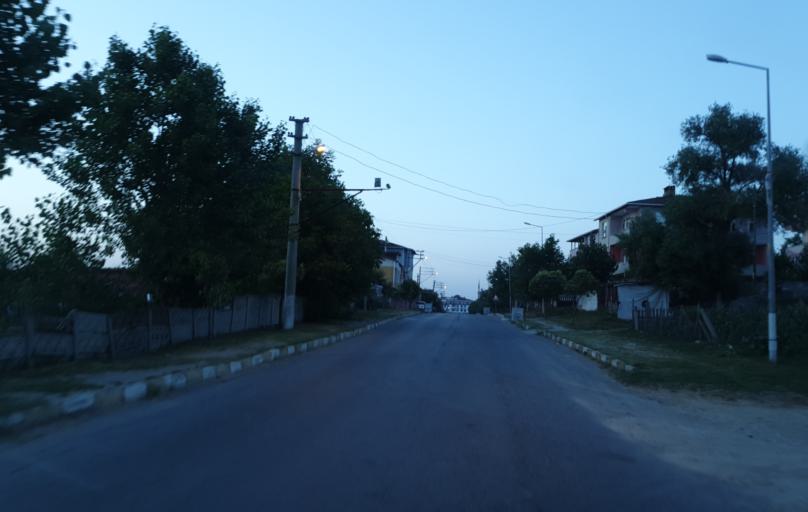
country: TR
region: Tekirdag
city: Saray
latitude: 41.3687
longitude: 27.9292
